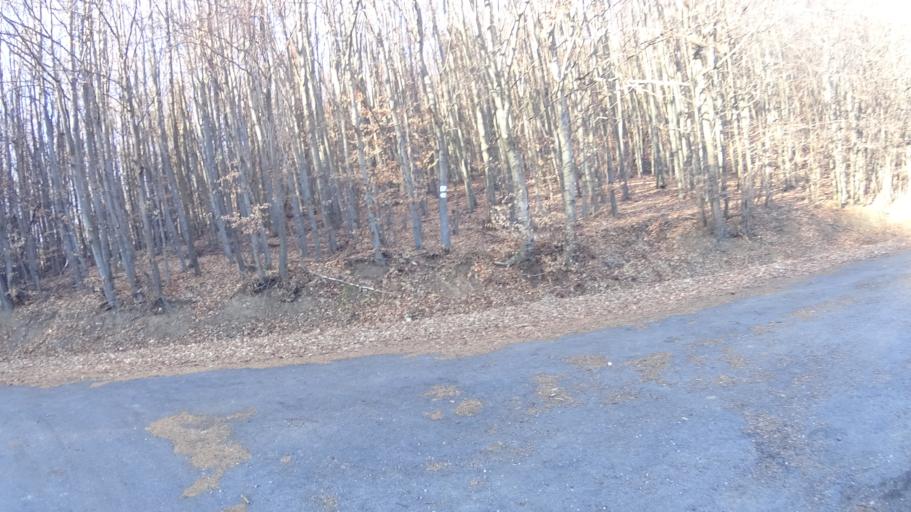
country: HU
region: Heves
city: Paradsasvar
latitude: 47.8995
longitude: 19.9295
